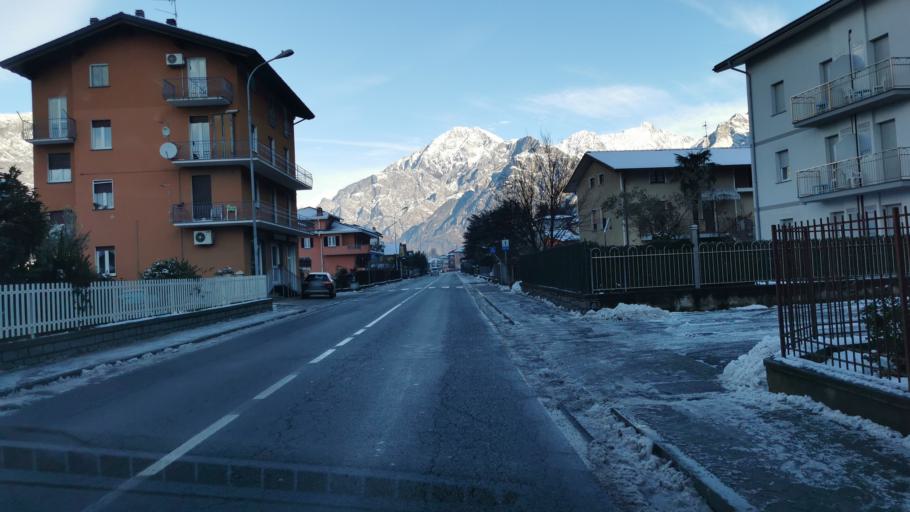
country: IT
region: Lombardy
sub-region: Provincia di Sondrio
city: Dubino
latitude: 46.1678
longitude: 9.4321
